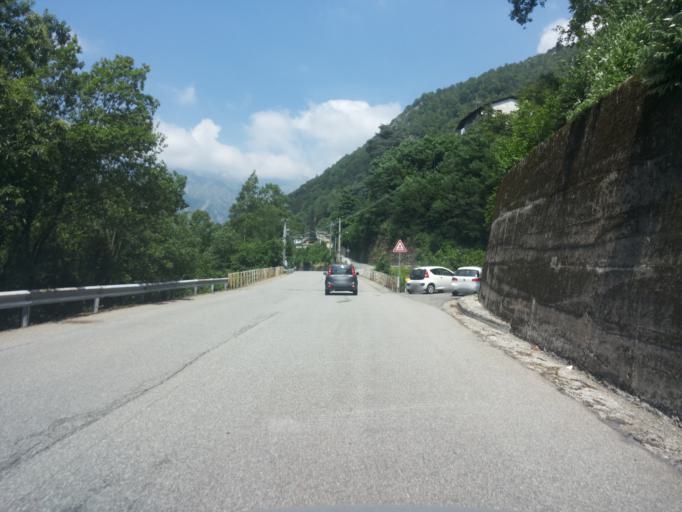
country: IT
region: Piedmont
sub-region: Provincia di Biella
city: Campiglia Cervo
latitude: 45.6694
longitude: 7.9909
